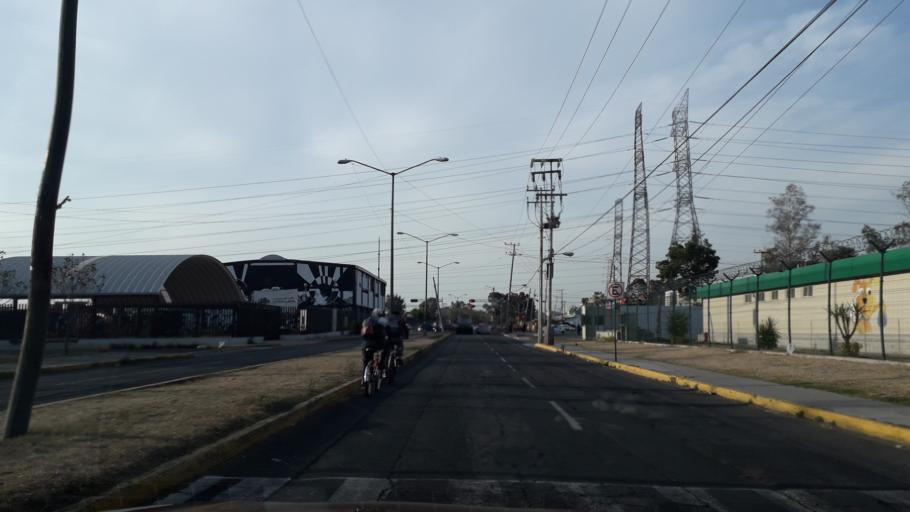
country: MX
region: Mexico City
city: Iztapalapa
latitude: 19.3610
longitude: -99.0489
